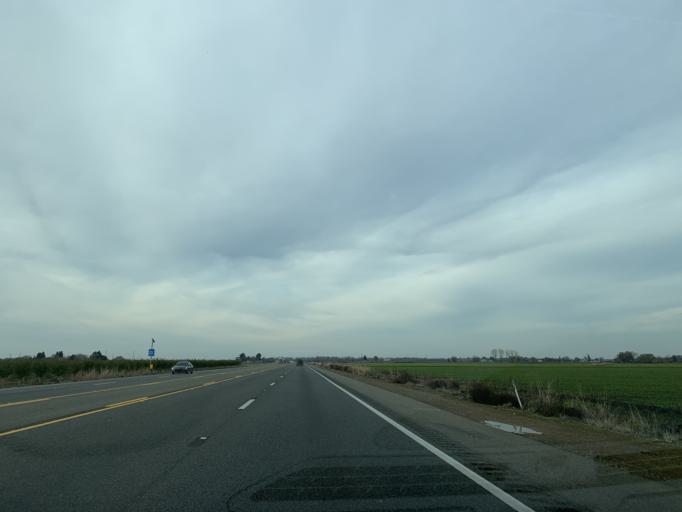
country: US
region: California
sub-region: Yuba County
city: Plumas Lake
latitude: 38.8753
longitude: -121.5618
